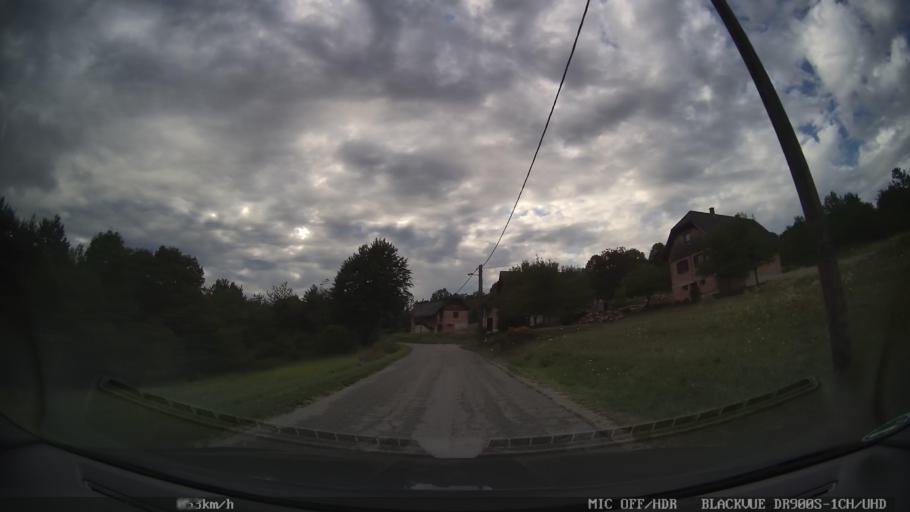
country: HR
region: Licko-Senjska
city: Jezerce
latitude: 44.9242
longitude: 15.5917
